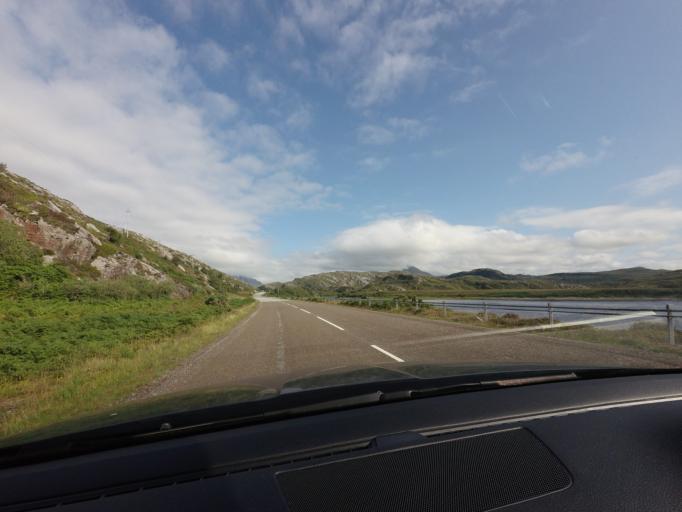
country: GB
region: Scotland
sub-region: Highland
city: Ullapool
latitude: 58.3798
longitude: -5.0296
